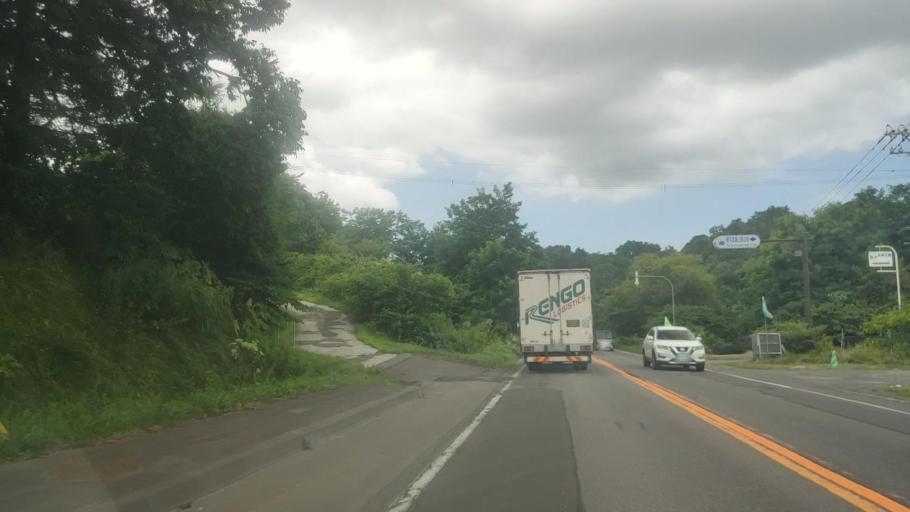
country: JP
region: Hokkaido
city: Nanae
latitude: 42.1171
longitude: 140.5384
